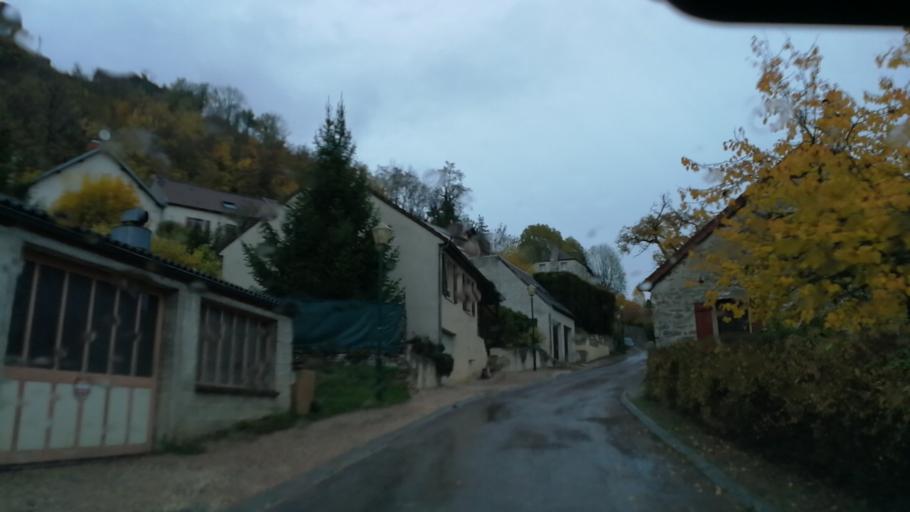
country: FR
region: Bourgogne
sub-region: Departement de la Cote-d'Or
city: Fleurey-sur-Ouche
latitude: 47.3254
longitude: 4.7891
